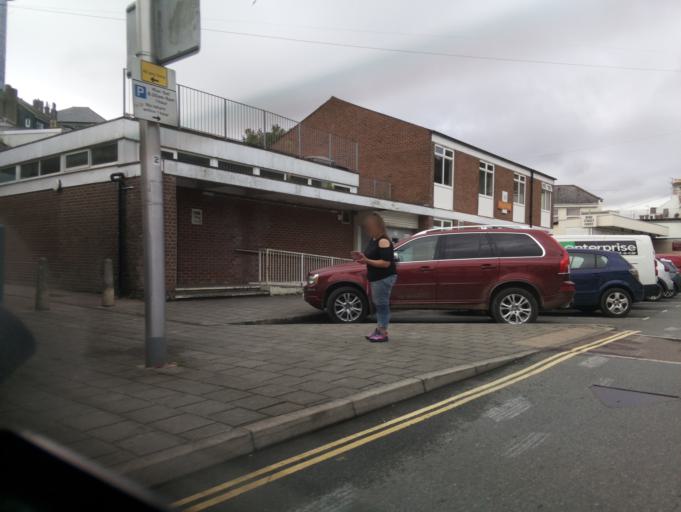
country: GB
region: England
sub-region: Devon
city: Kingsbridge
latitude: 50.2839
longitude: -3.7766
